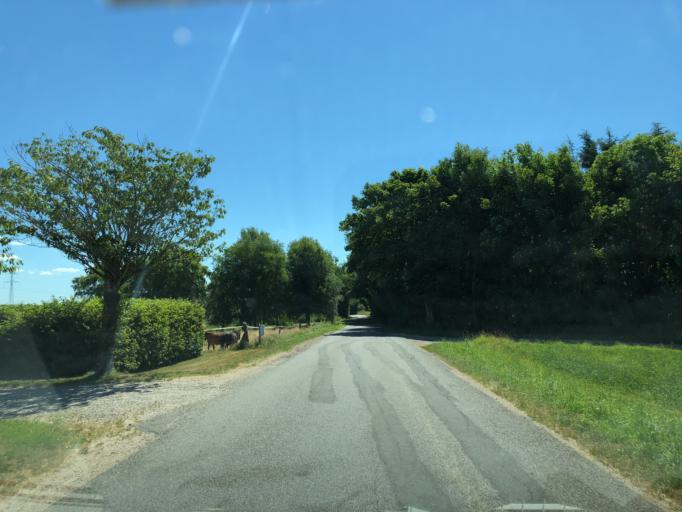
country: DK
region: Central Jutland
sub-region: Viborg Kommune
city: Viborg
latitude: 56.5184
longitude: 9.4907
